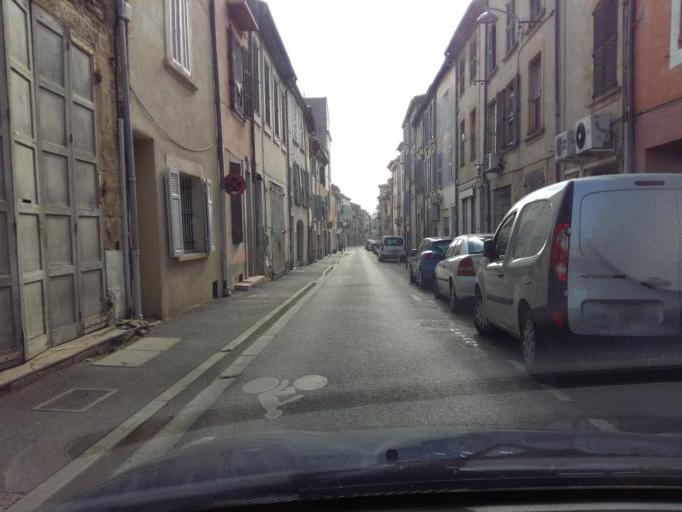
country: FR
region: Provence-Alpes-Cote d'Azur
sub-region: Departement des Bouches-du-Rhone
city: Salon-de-Provence
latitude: 43.6401
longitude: 5.0995
